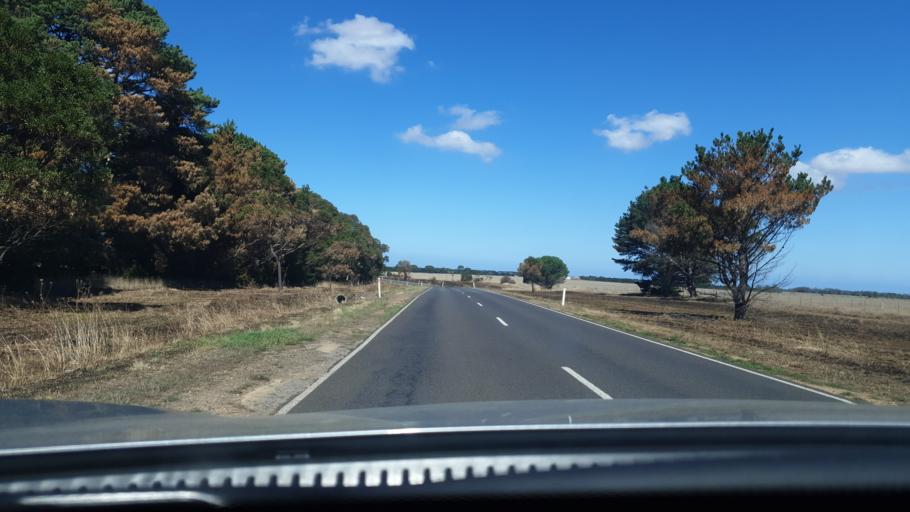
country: AU
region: Victoria
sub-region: Warrnambool
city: Warrnambool
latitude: -38.1657
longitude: 142.3974
